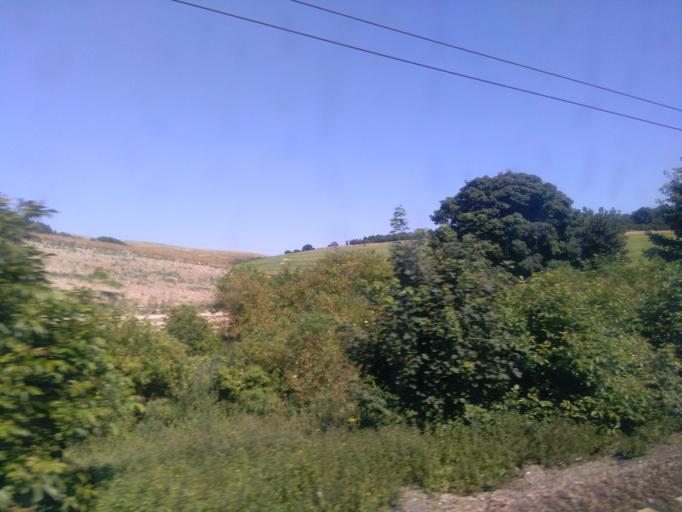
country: GB
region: England
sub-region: Luton
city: Luton
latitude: 51.8686
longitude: -0.3887
